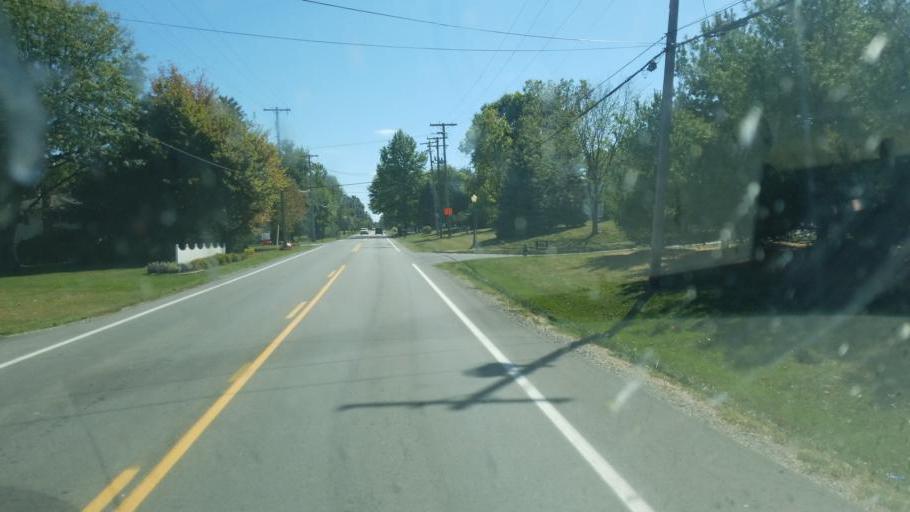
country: US
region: Ohio
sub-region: Huron County
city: Plymouth
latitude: 41.0062
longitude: -82.6708
